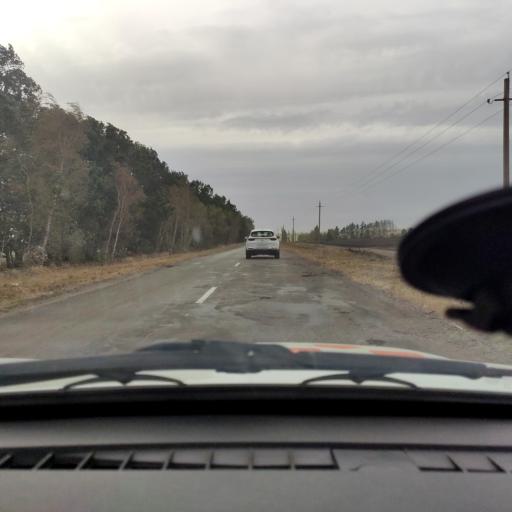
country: RU
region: Lipetsk
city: Khlevnoye
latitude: 52.0057
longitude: 39.1351
